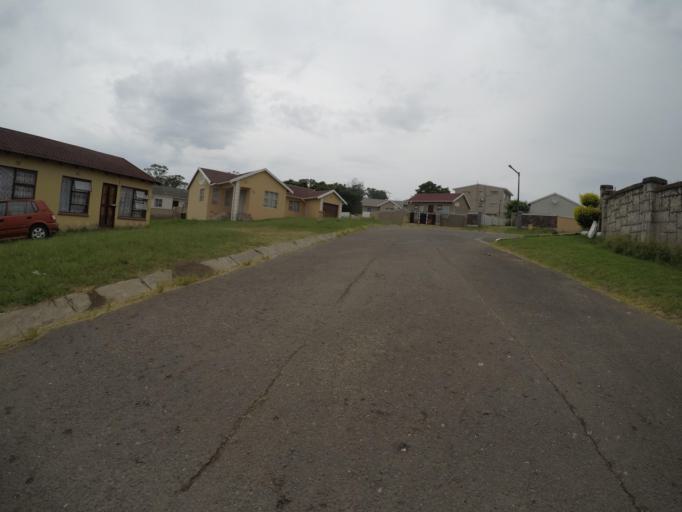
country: ZA
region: Eastern Cape
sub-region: Buffalo City Metropolitan Municipality
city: East London
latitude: -32.9693
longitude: 27.8331
